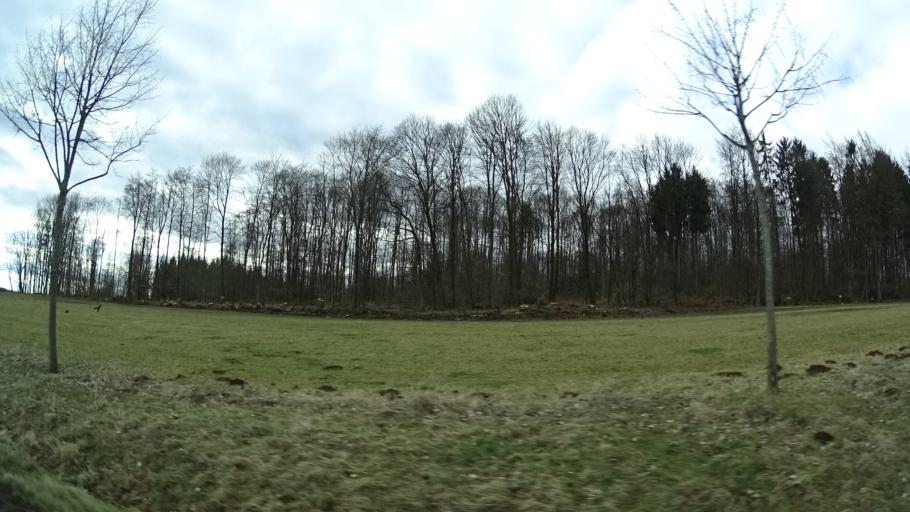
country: DE
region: Hesse
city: Gedern
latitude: 50.4403
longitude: 9.2037
